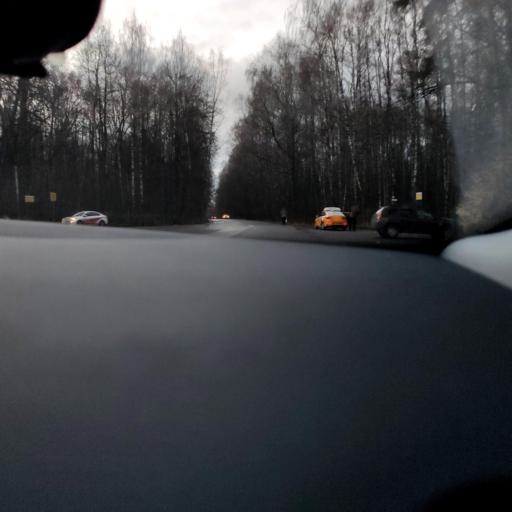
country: RU
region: Moskovskaya
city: Bogorodskoye
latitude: 55.8333
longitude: 37.7449
